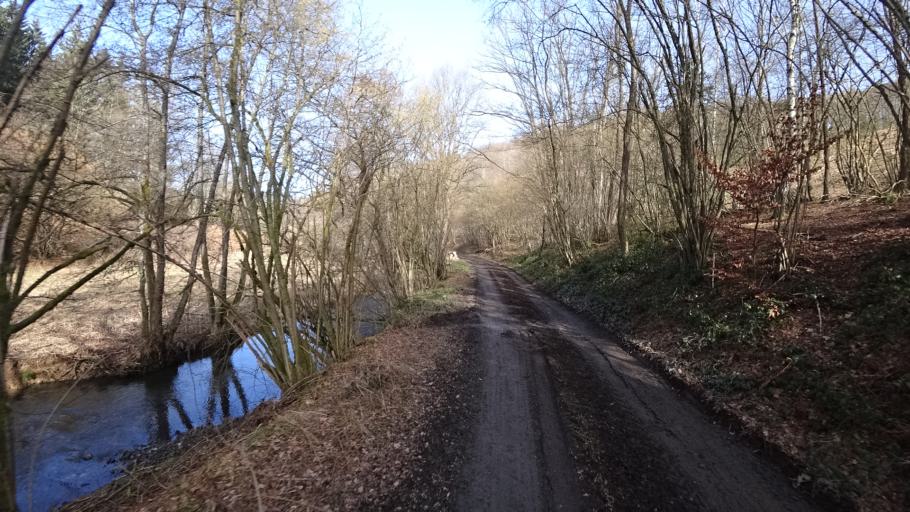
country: DE
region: Rheinland-Pfalz
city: Scheuerfeld
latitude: 50.7714
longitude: 7.8347
